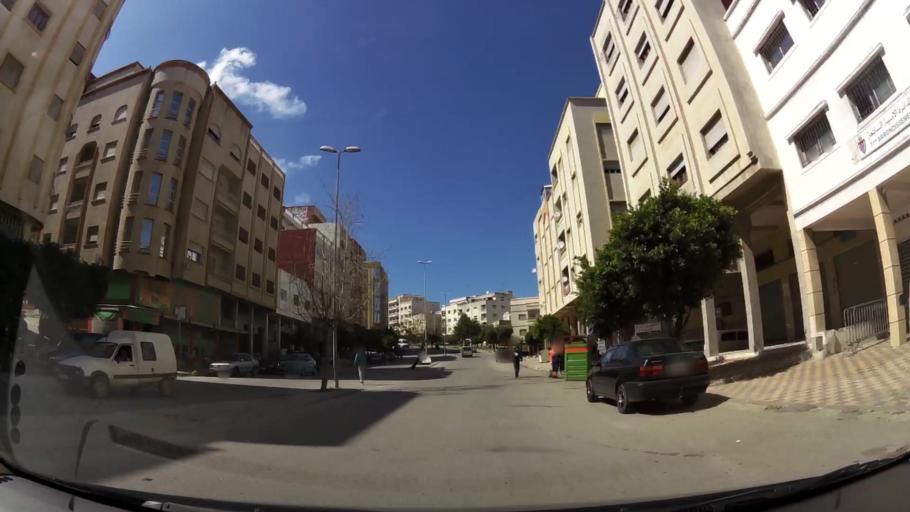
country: MA
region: Tanger-Tetouan
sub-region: Tanger-Assilah
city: Tangier
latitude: 35.7489
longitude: -5.8136
